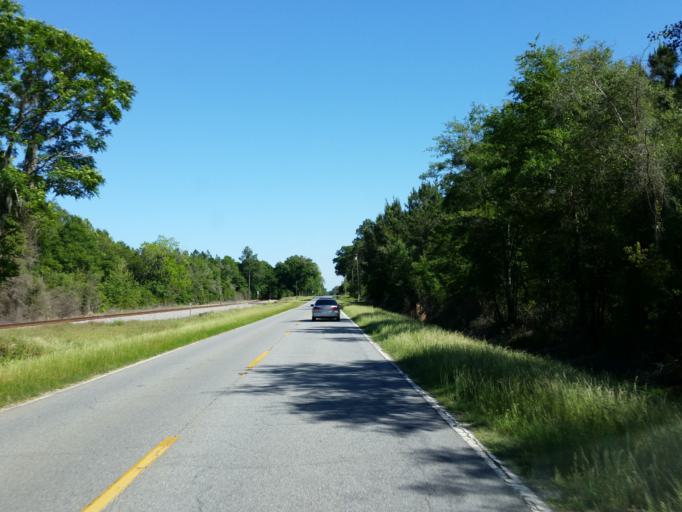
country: US
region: Georgia
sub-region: Echols County
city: Statenville
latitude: 30.6443
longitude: -83.1390
